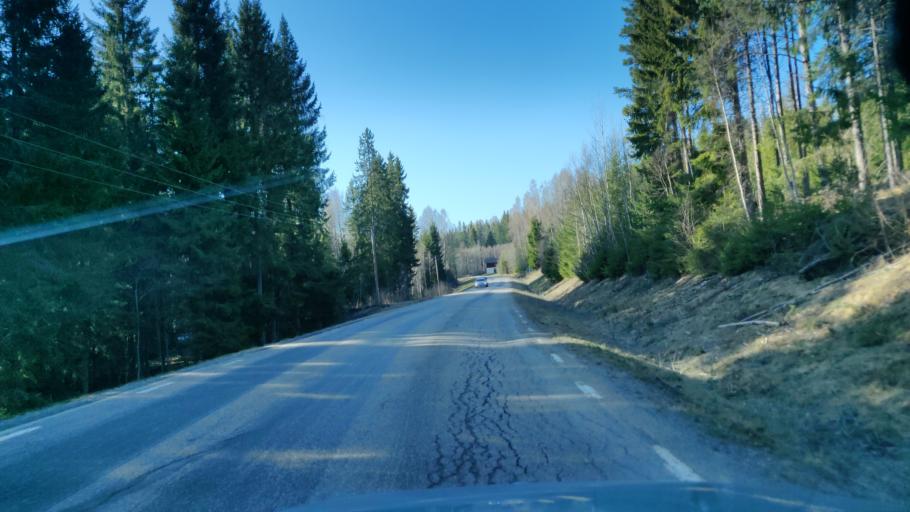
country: SE
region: Vaermland
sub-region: Munkfors Kommun
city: Munkfors
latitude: 59.9815
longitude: 13.4049
